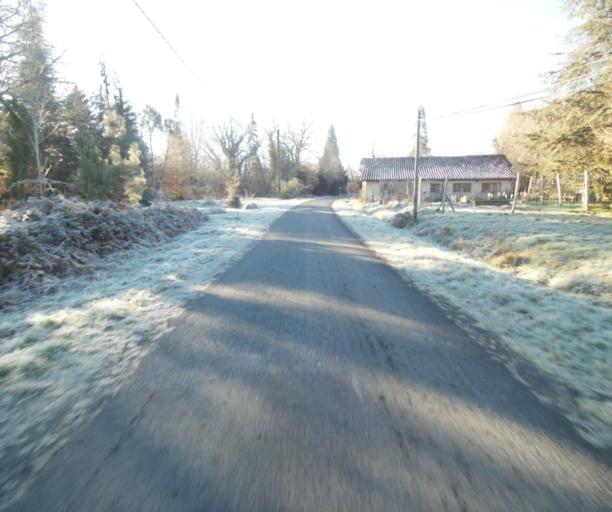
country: FR
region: Aquitaine
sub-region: Departement des Landes
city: Gabarret
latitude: 44.0991
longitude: 0.0532
